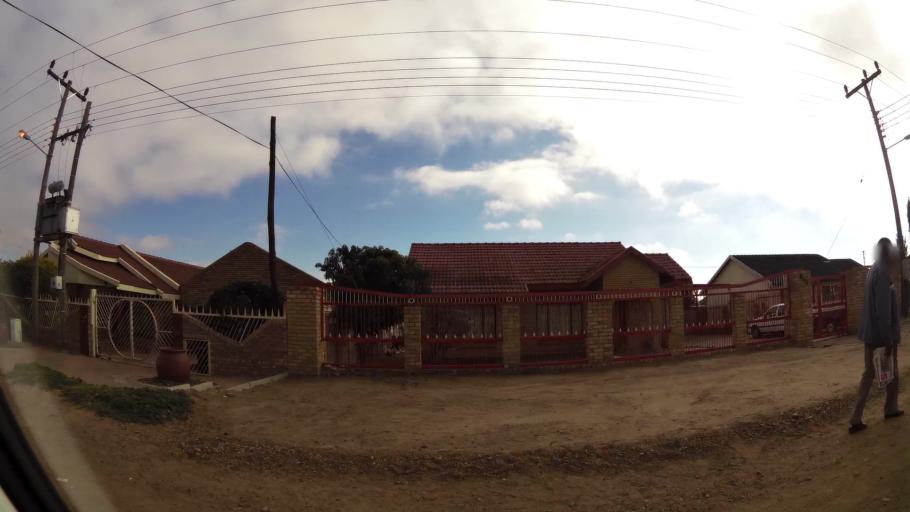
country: ZA
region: Limpopo
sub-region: Capricorn District Municipality
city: Polokwane
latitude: -23.8433
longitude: 29.3797
